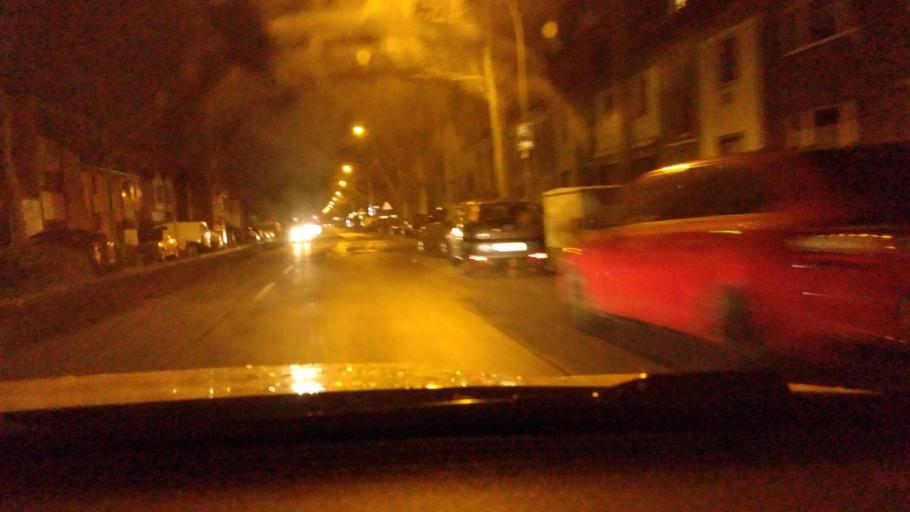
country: DE
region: North Rhine-Westphalia
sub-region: Regierungsbezirk Koln
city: Bayenthal
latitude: 50.9006
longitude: 6.9483
